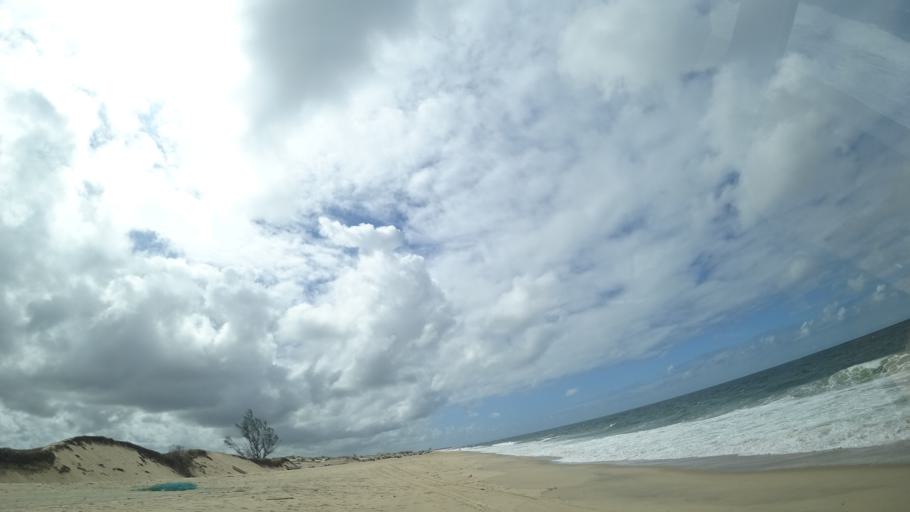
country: MZ
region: Sofala
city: Beira
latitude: -19.6174
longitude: 35.2183
